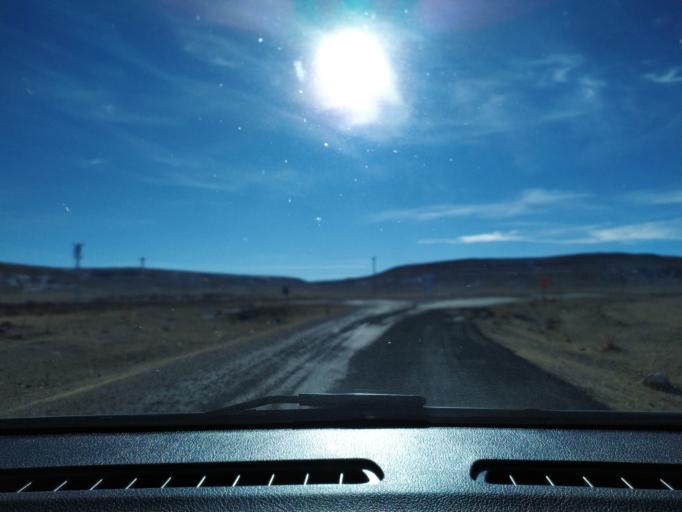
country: TR
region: Kayseri
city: Orensehir
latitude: 39.0979
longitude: 36.6982
